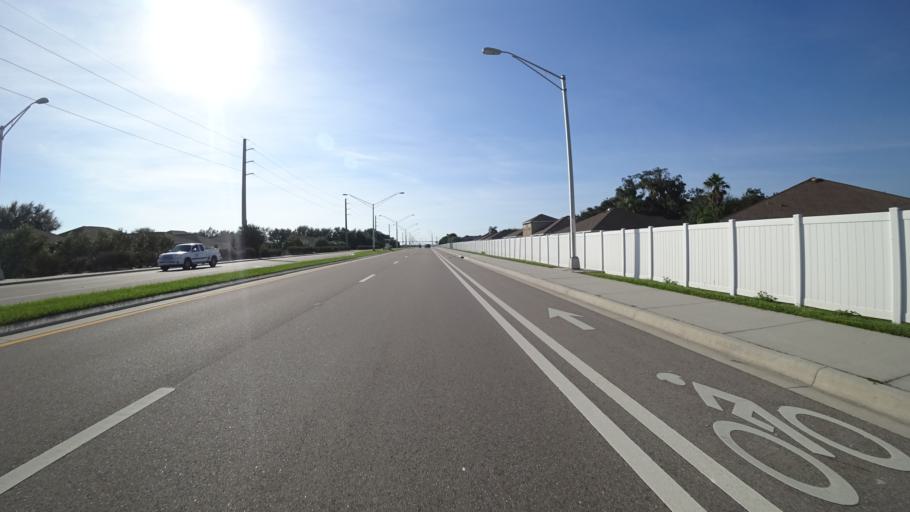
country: US
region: Florida
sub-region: Manatee County
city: Samoset
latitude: 27.4616
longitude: -82.5218
